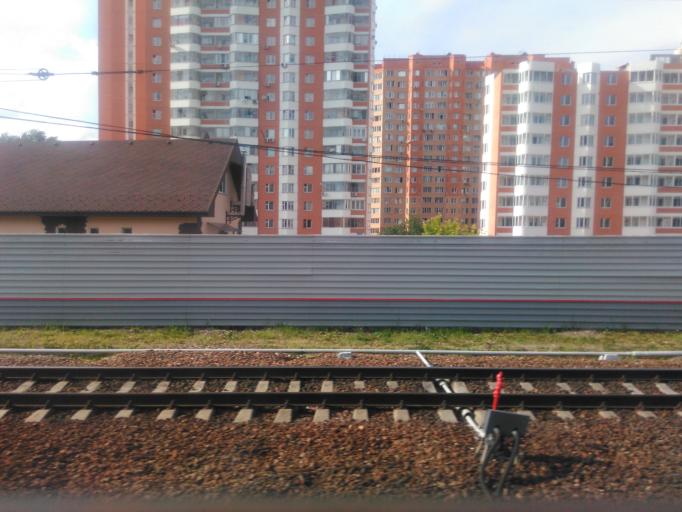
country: RU
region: Moskovskaya
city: Zheleznodorozhnyy
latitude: 55.7525
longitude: 37.9988
